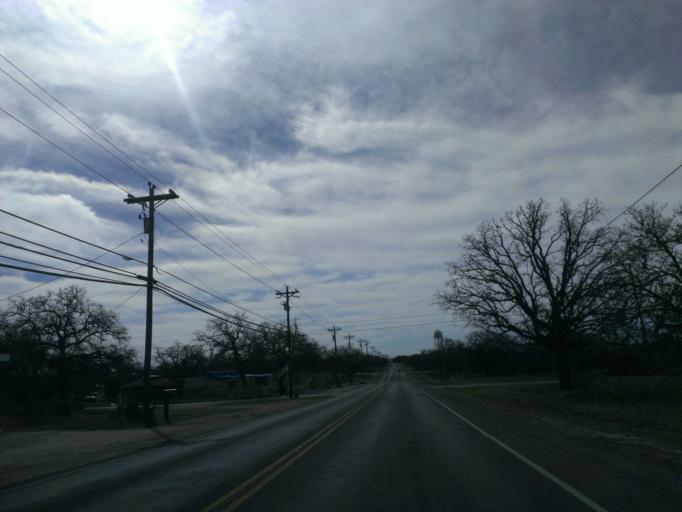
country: US
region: Texas
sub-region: Burnet County
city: Granite Shoals
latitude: 30.5947
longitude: -98.3828
